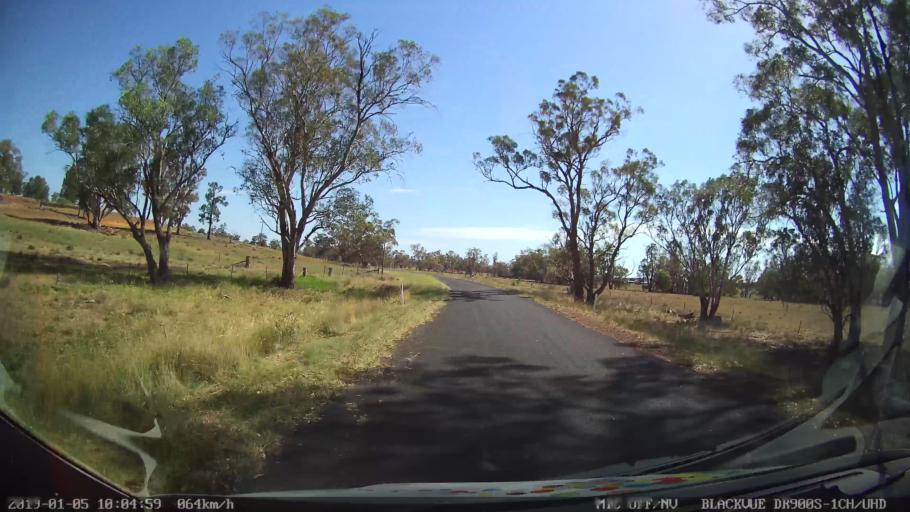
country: AU
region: New South Wales
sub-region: Gilgandra
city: Gilgandra
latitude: -31.6703
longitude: 148.8632
